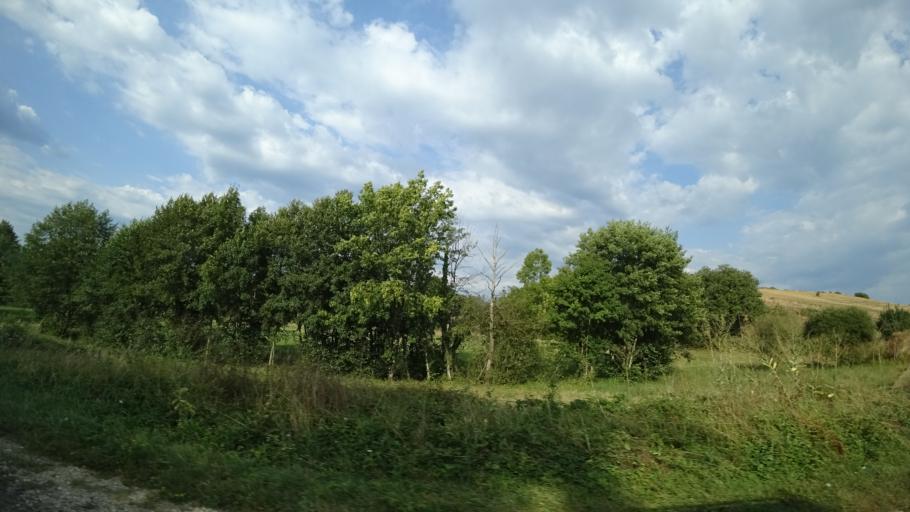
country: FR
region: Midi-Pyrenees
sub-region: Departement de l'Aveyron
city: Saint-Christophe-Vallon
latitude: 44.4918
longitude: 2.3885
